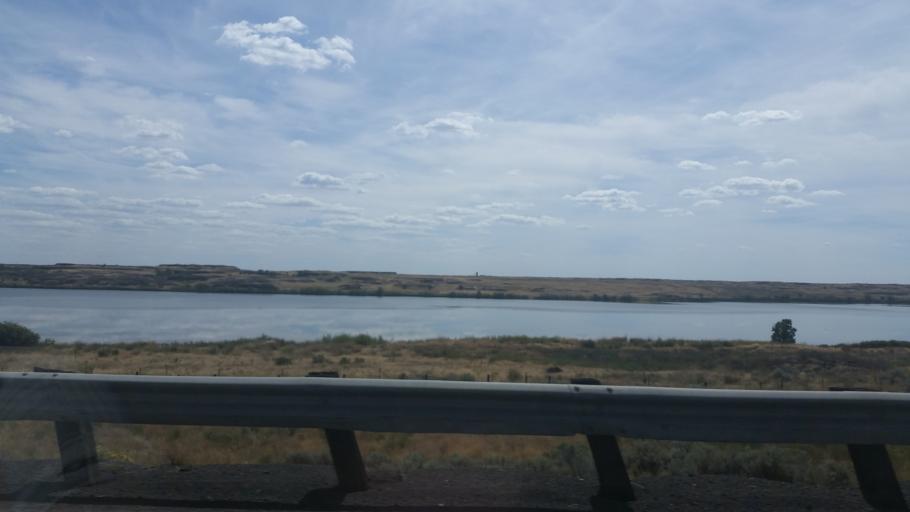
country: US
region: Washington
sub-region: Adams County
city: Ritzville
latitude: 47.2775
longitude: -118.0525
